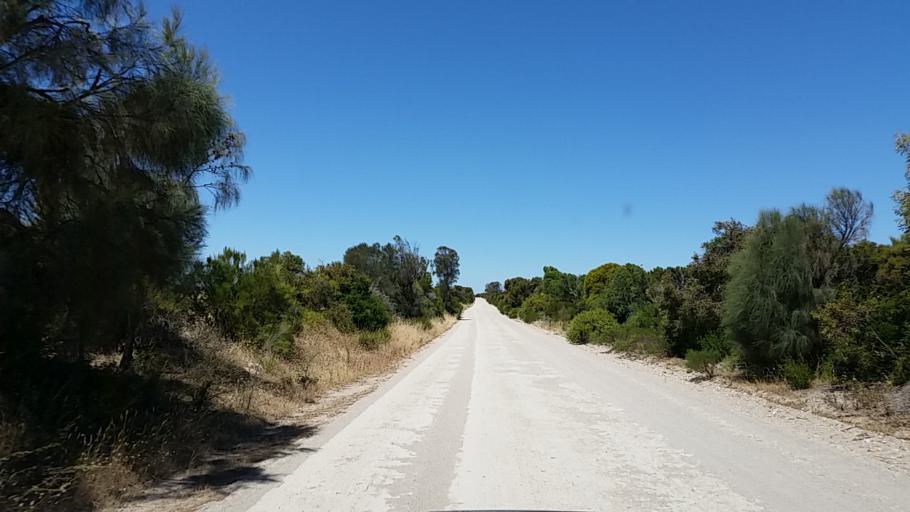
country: AU
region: South Australia
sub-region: Yorke Peninsula
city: Honiton
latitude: -35.0928
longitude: 137.4396
